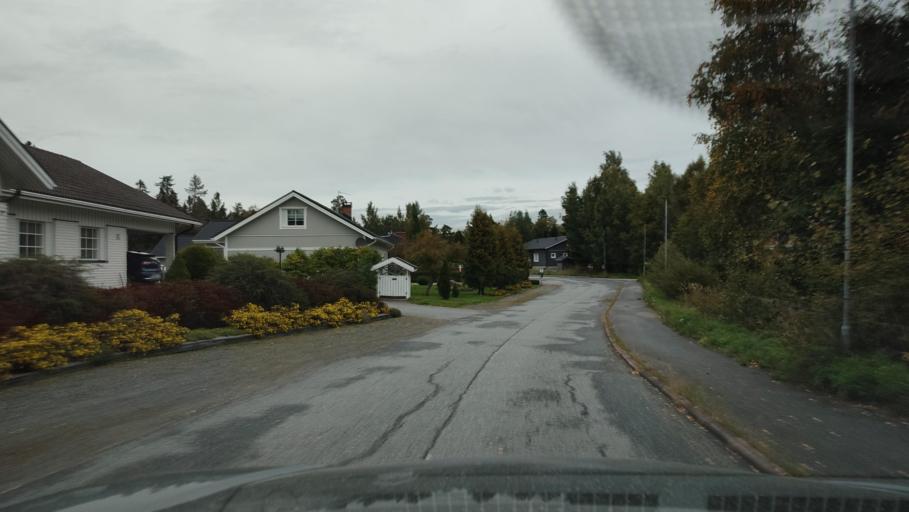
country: FI
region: Ostrobothnia
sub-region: Sydosterbotten
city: Kristinestad
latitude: 62.2801
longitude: 21.3523
